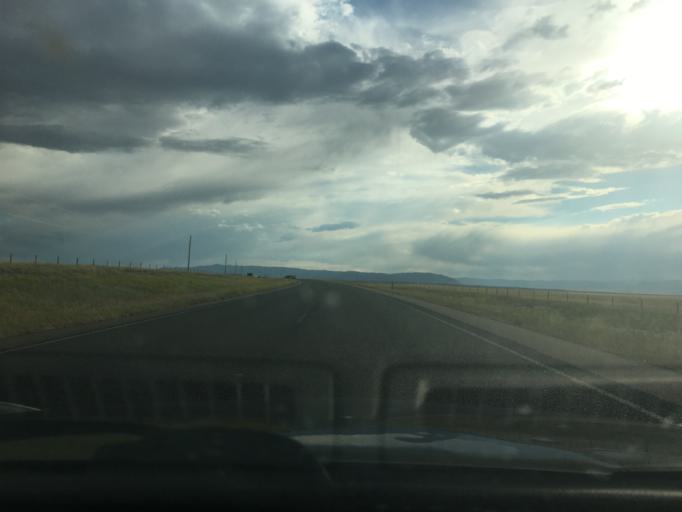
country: US
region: Wyoming
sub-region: Albany County
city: Laramie
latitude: 41.3192
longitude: -105.7650
